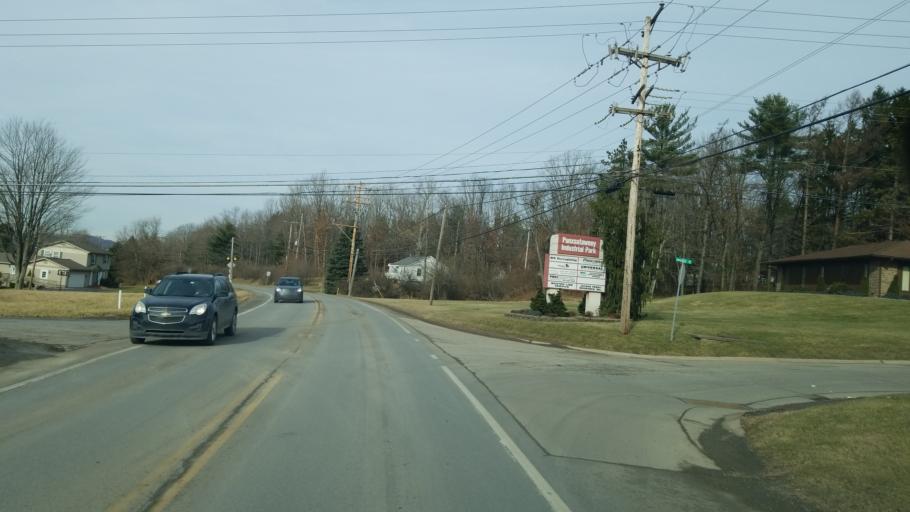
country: US
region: Pennsylvania
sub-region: Jefferson County
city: Punxsutawney
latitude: 40.9330
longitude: -78.9878
